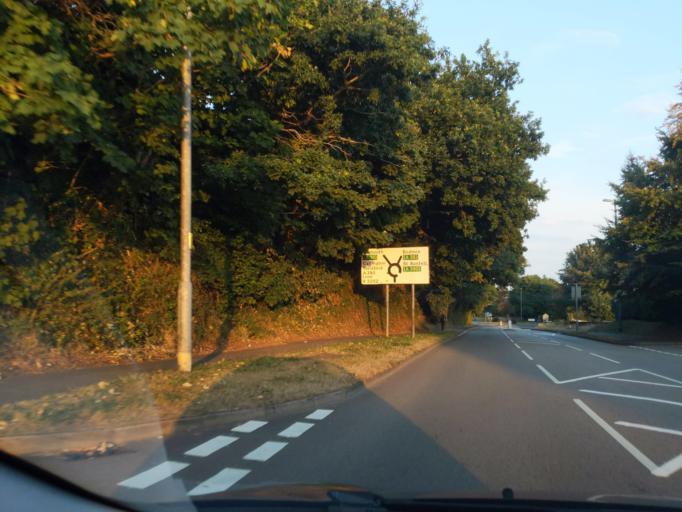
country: GB
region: England
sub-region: Cornwall
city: Liskeard
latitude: 50.4516
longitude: -4.4559
